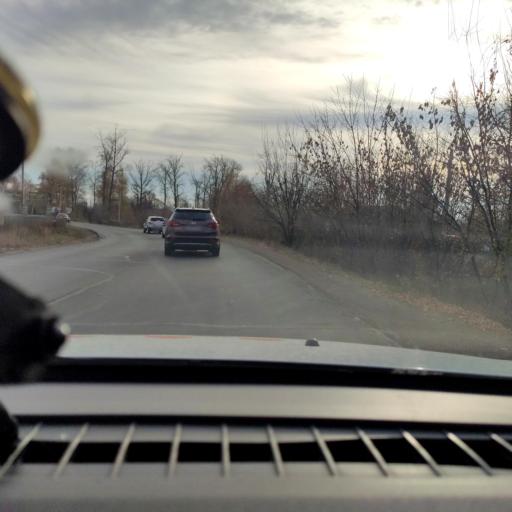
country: RU
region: Samara
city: Novokuybyshevsk
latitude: 53.1452
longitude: 50.0153
